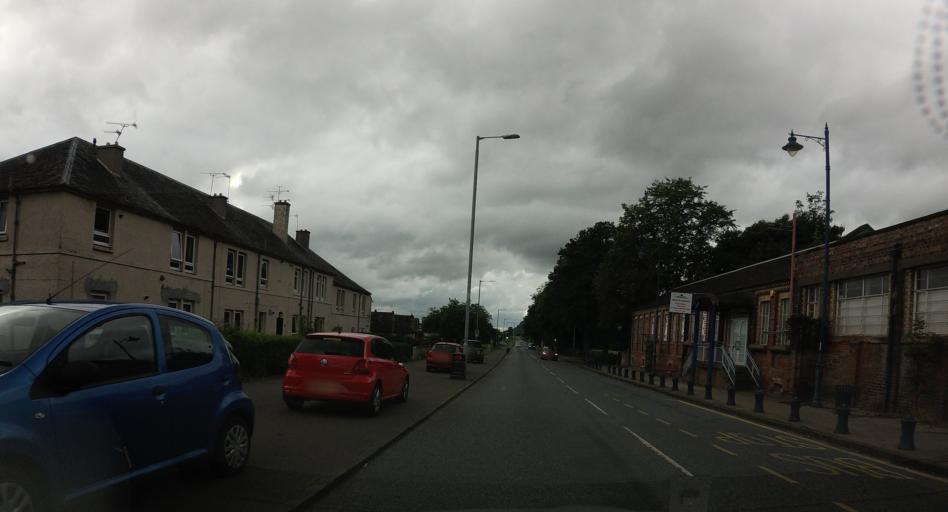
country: GB
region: Scotland
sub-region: Clackmannanshire
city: Alva
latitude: 56.1528
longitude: -3.8075
